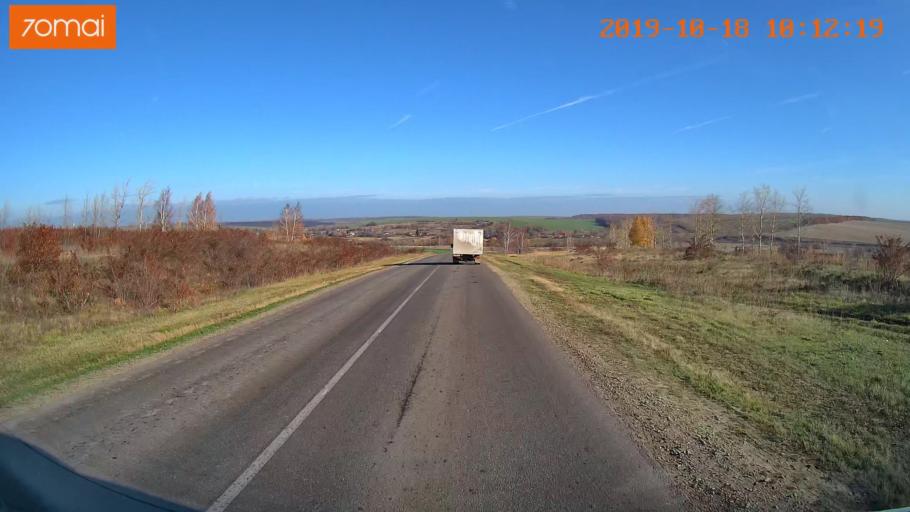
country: RU
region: Tula
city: Kurkino
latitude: 53.3927
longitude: 38.5068
